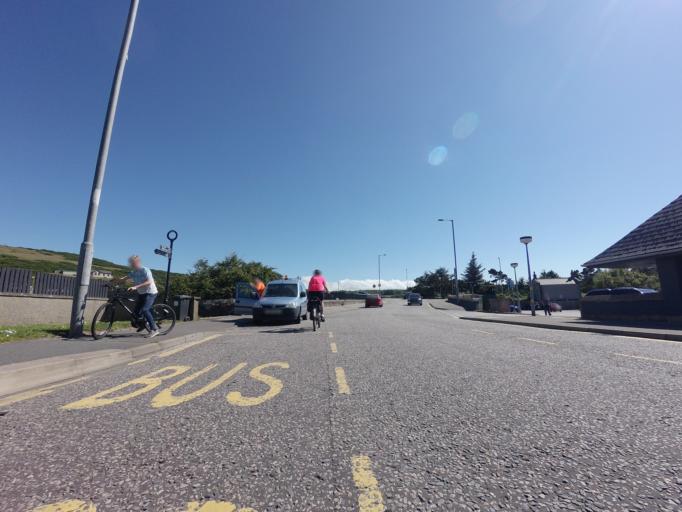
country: GB
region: Scotland
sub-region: Aberdeenshire
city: Banff
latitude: 57.6634
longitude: -2.5148
